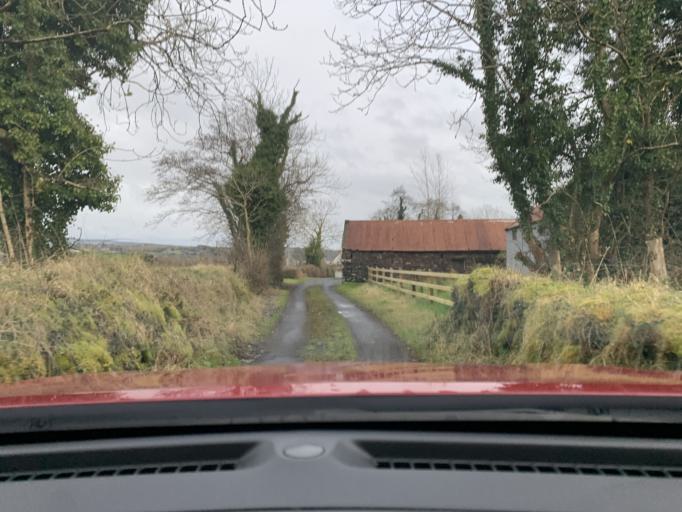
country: IE
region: Connaught
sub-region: Sligo
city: Ballymote
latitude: 53.9700
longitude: -8.4720
